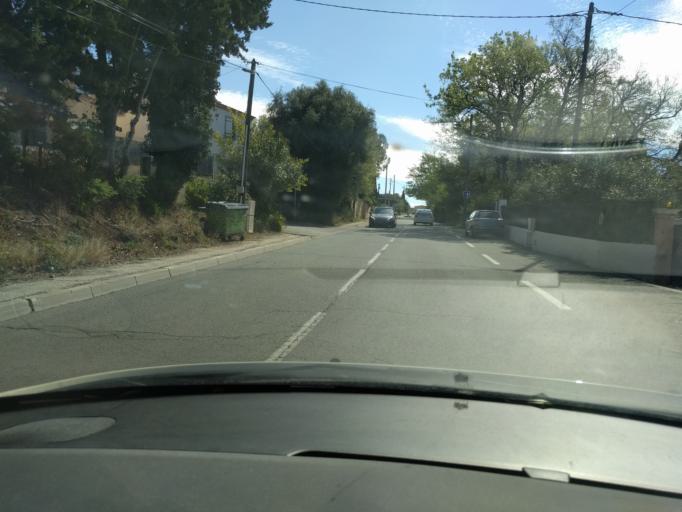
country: FR
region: Provence-Alpes-Cote d'Azur
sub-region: Departement du Var
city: Pierrefeu-du-Var
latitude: 43.2252
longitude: 6.1369
